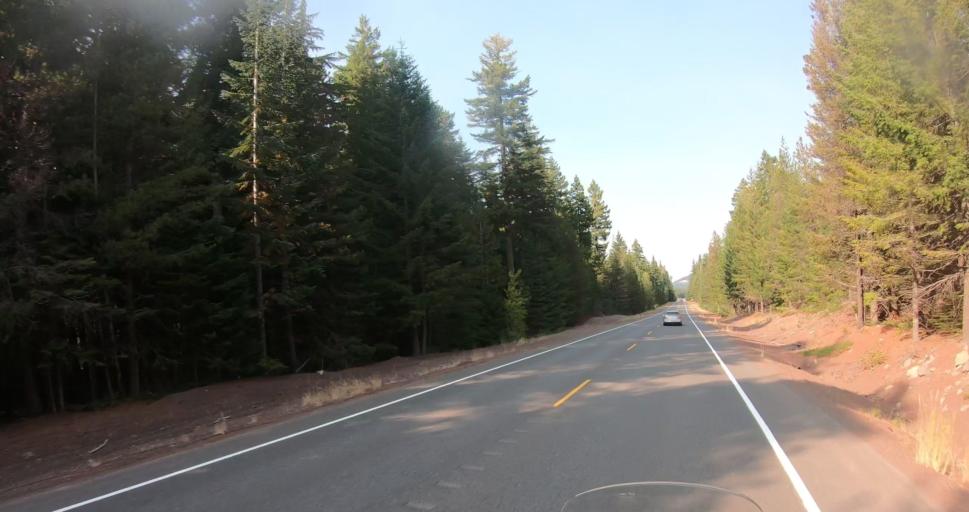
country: US
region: Oregon
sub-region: Hood River County
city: Odell
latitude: 45.3529
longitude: -121.5680
